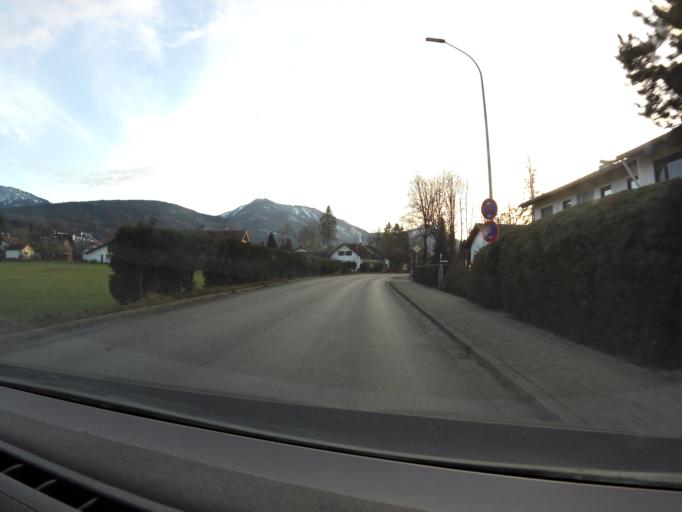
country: DE
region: Bavaria
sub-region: Upper Bavaria
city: Benediktbeuern
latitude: 47.7052
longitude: 11.4109
